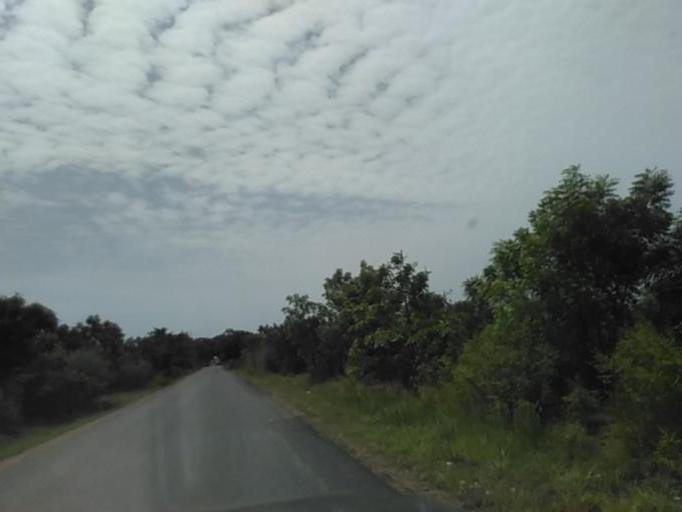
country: GH
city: Akropong
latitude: 6.0930
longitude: 0.0727
